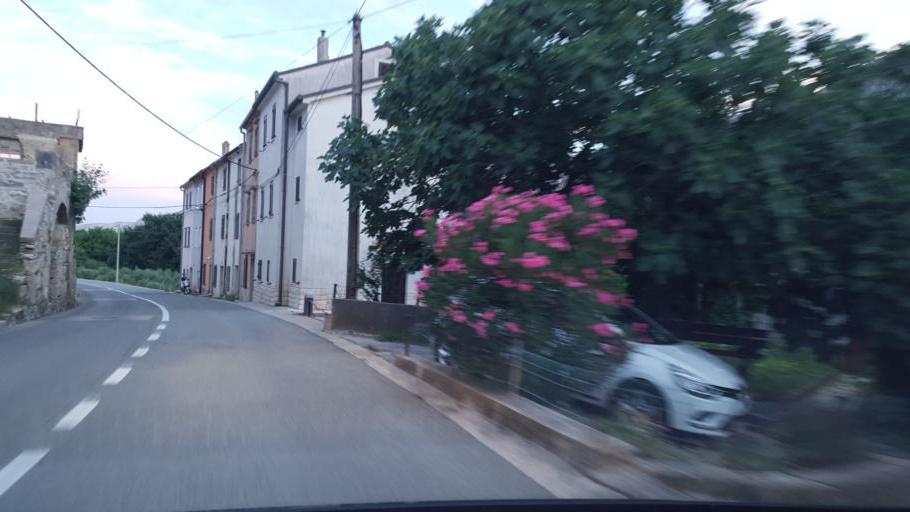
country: HR
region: Primorsko-Goranska
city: Punat
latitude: 44.9979
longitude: 14.7120
